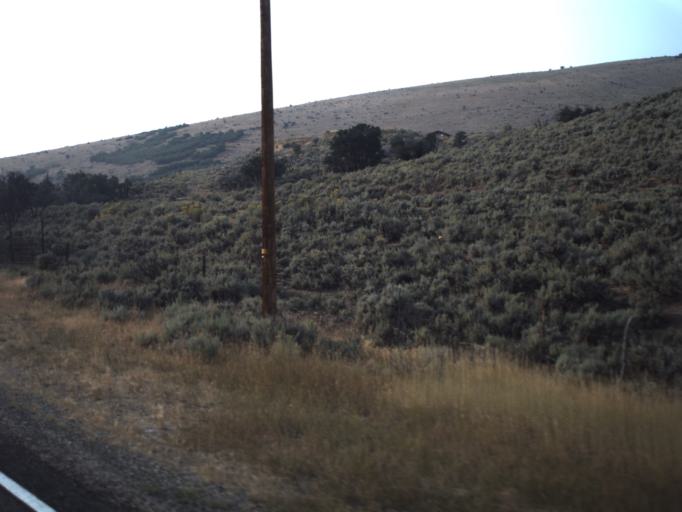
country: US
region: Utah
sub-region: Summit County
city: Kamas
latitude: 40.6402
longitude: -111.2633
